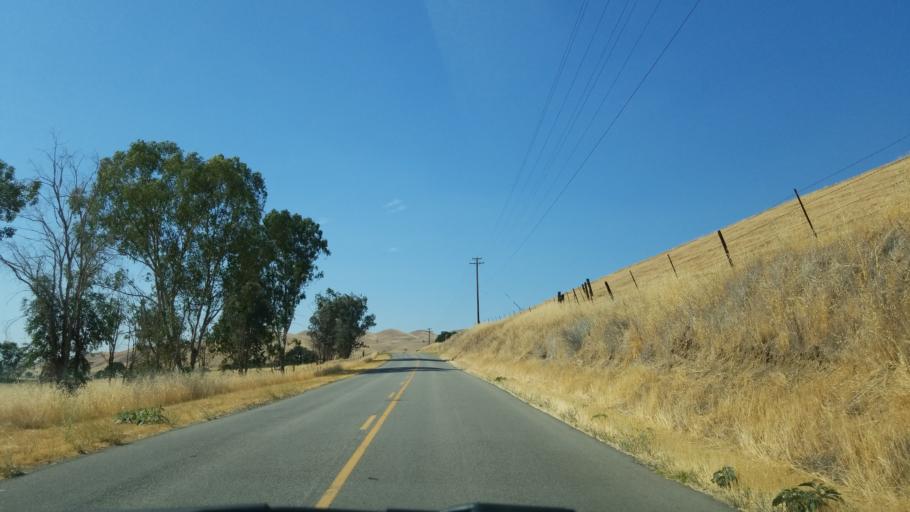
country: US
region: California
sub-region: San Luis Obispo County
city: San Miguel
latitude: 35.7639
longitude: -120.6861
